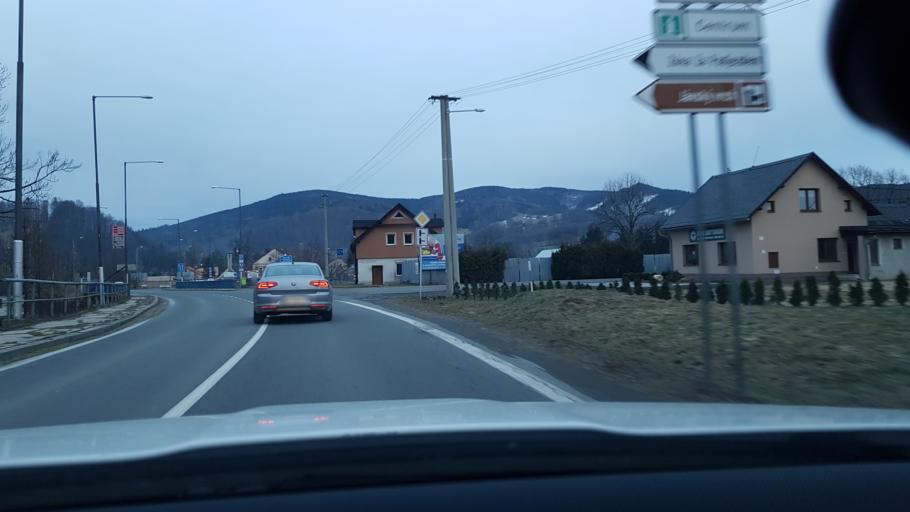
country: CZ
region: Olomoucky
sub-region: Okres Jesenik
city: Jesenik
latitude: 50.2122
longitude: 17.1997
